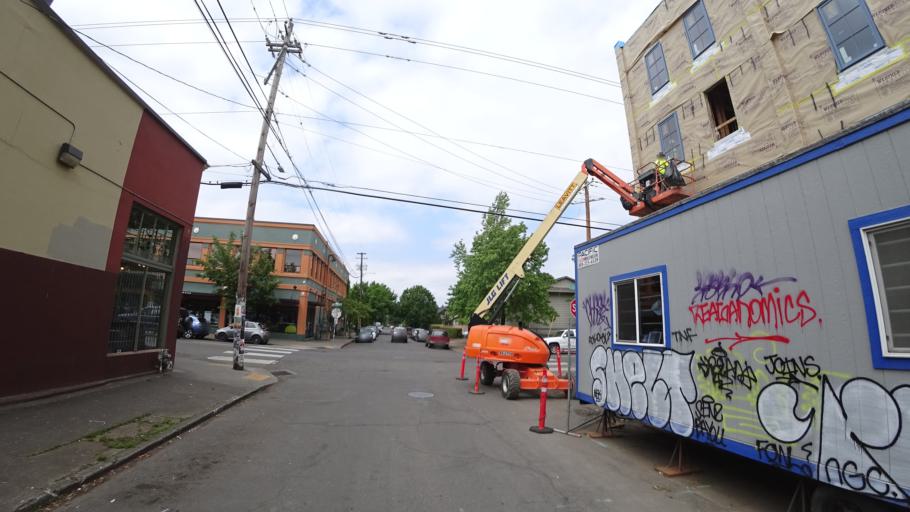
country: US
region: Oregon
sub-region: Multnomah County
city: Portland
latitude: 45.5589
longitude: -122.6459
